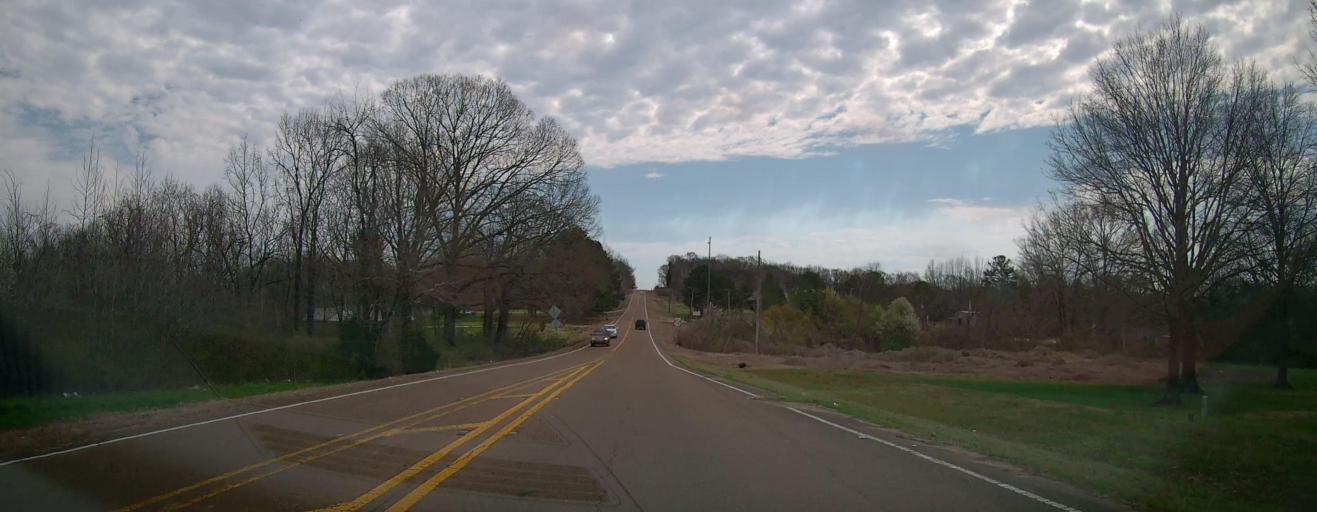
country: US
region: Mississippi
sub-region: Marshall County
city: Byhalia
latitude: 34.8457
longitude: -89.6164
